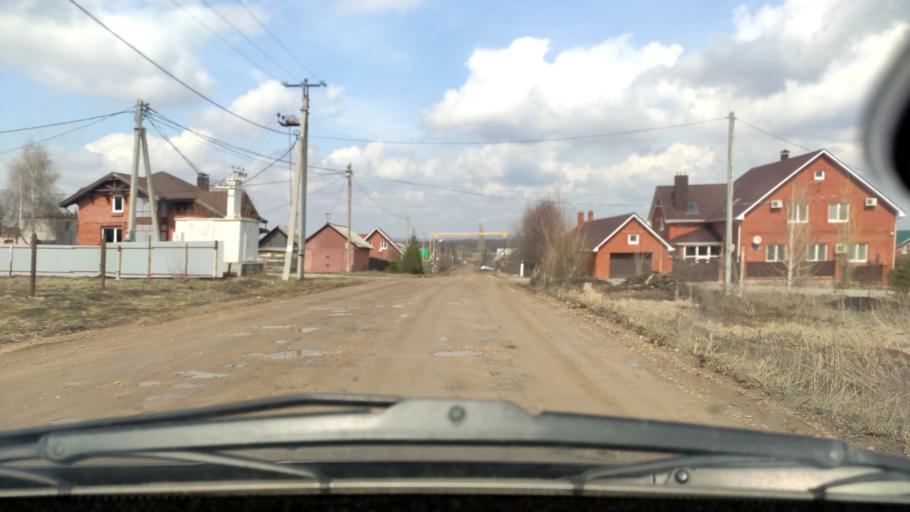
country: RU
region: Bashkortostan
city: Iglino
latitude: 54.7957
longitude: 56.2746
